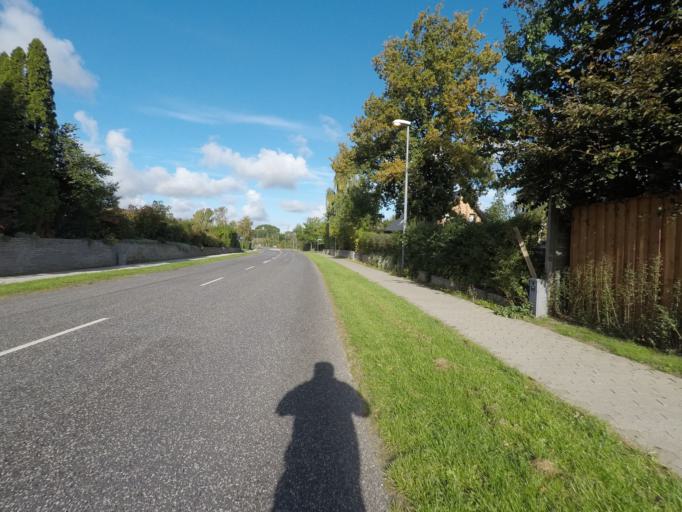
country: DK
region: Capital Region
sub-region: Egedal Kommune
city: Smorumnedre
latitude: 55.7375
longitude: 12.2947
